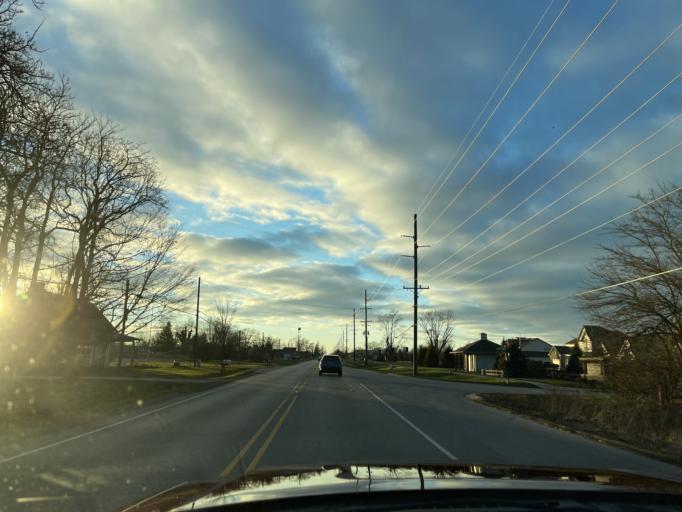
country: US
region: Indiana
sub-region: Hendricks County
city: Avon
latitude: 39.7620
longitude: -86.4545
